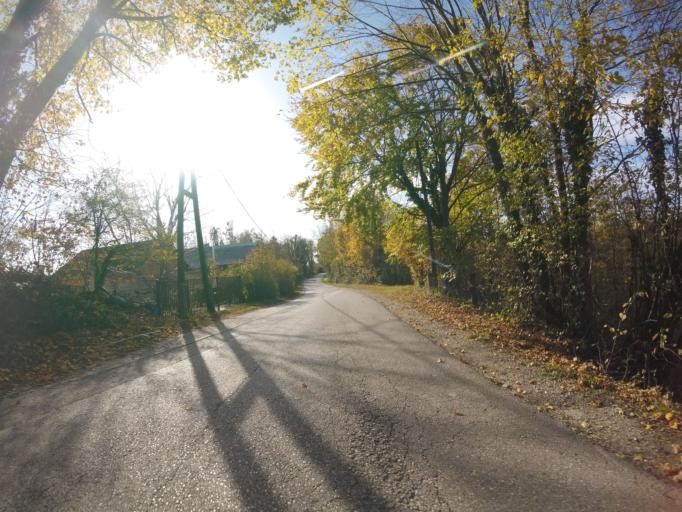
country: HR
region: Zagrebacka
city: Lukavec
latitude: 45.6127
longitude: 16.0059
